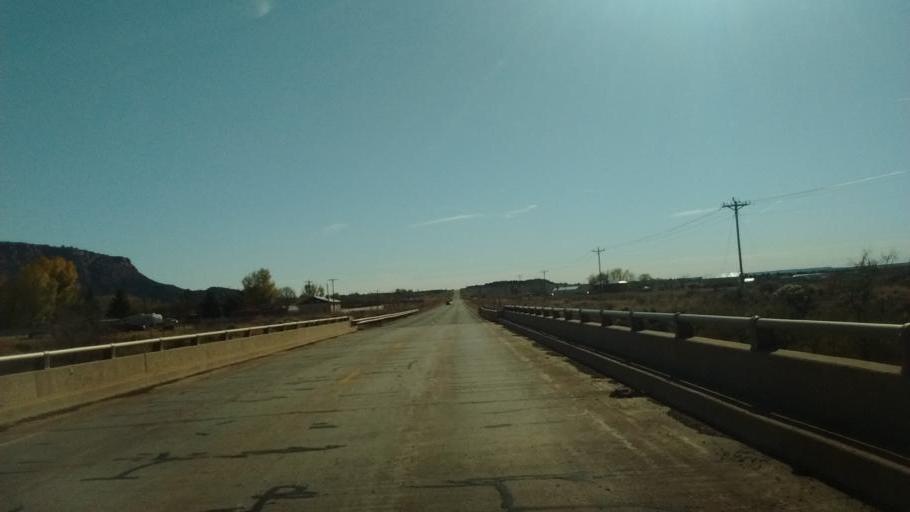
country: US
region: Arizona
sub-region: Mohave County
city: Colorado City
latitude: 36.9882
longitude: -112.9892
